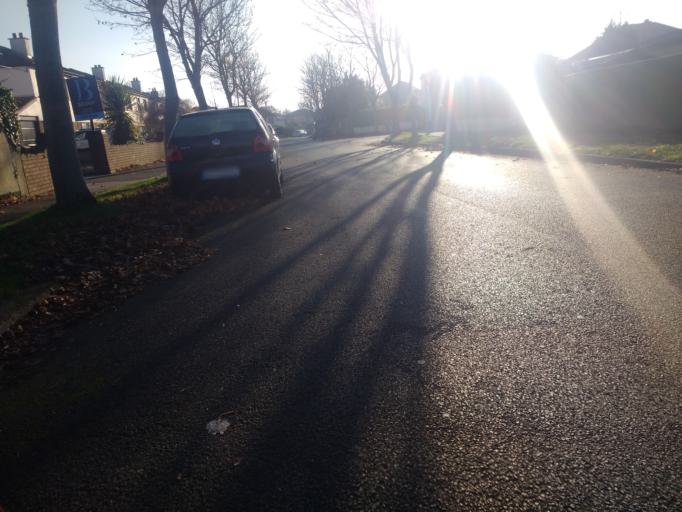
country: IE
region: Leinster
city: Kinsealy-Drinan
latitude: 53.4544
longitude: -6.1859
